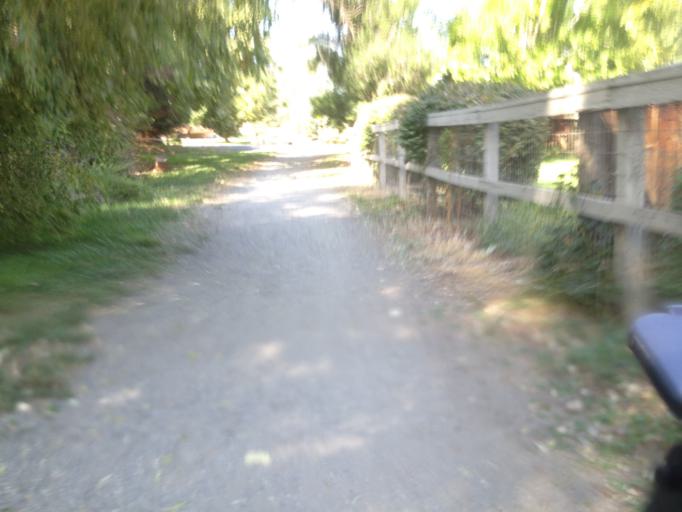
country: US
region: Colorado
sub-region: Boulder County
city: Louisville
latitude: 39.9943
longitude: -105.1214
